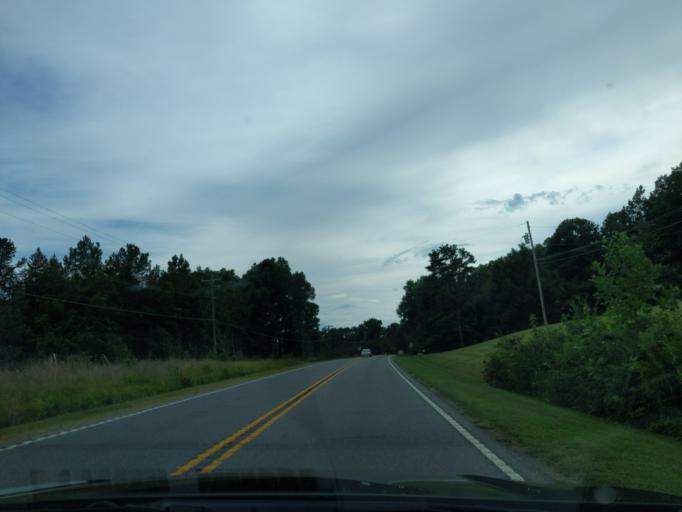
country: US
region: North Carolina
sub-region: Cabarrus County
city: Mount Pleasant
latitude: 35.4121
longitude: -80.4294
